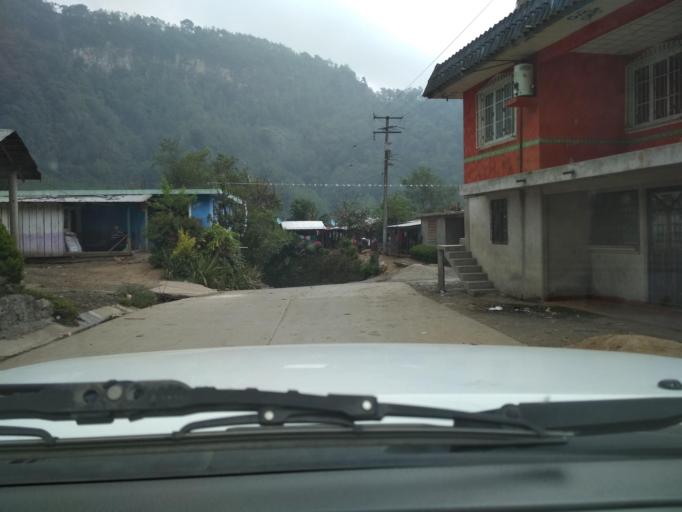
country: MX
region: Veracruz
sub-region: La Perla
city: Metlac Hernandez (Metlac Primero)
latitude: 18.9794
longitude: -97.1365
